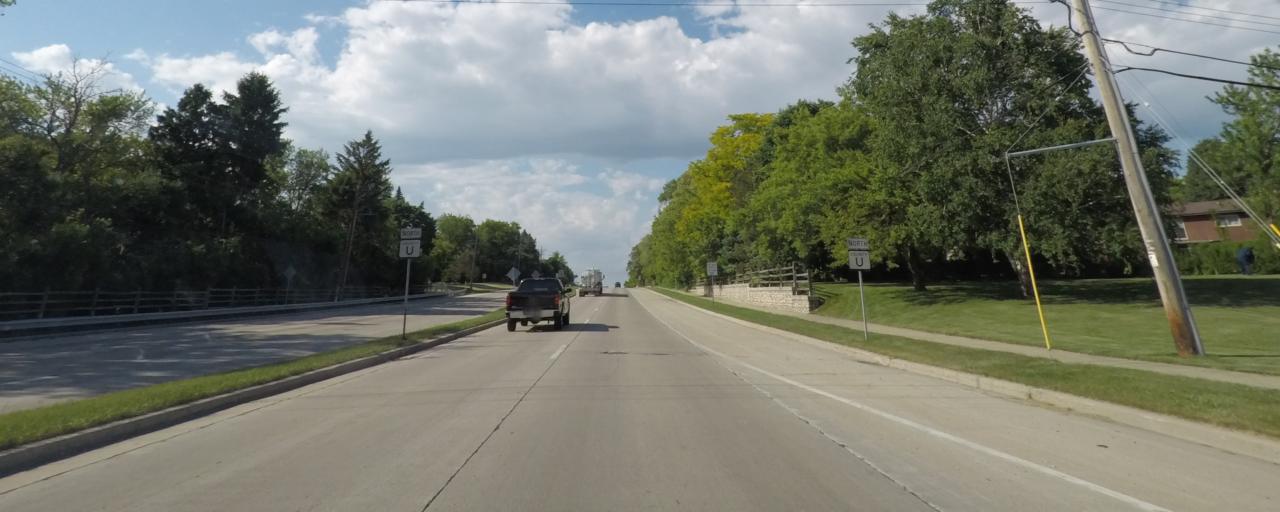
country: US
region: Wisconsin
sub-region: Milwaukee County
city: Greendale
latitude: 42.9384
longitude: -88.0087
